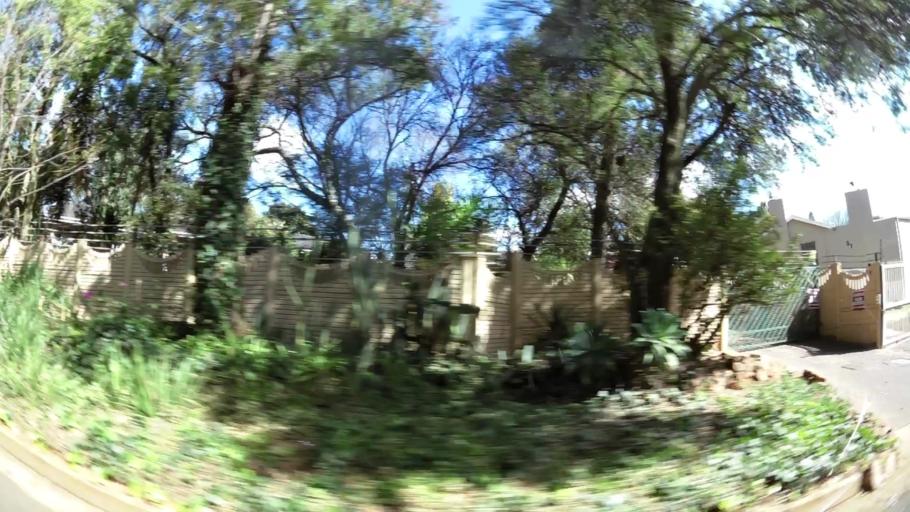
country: ZA
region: Gauteng
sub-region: West Rand District Municipality
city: Krugersdorp
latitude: -26.0903
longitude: 27.7963
